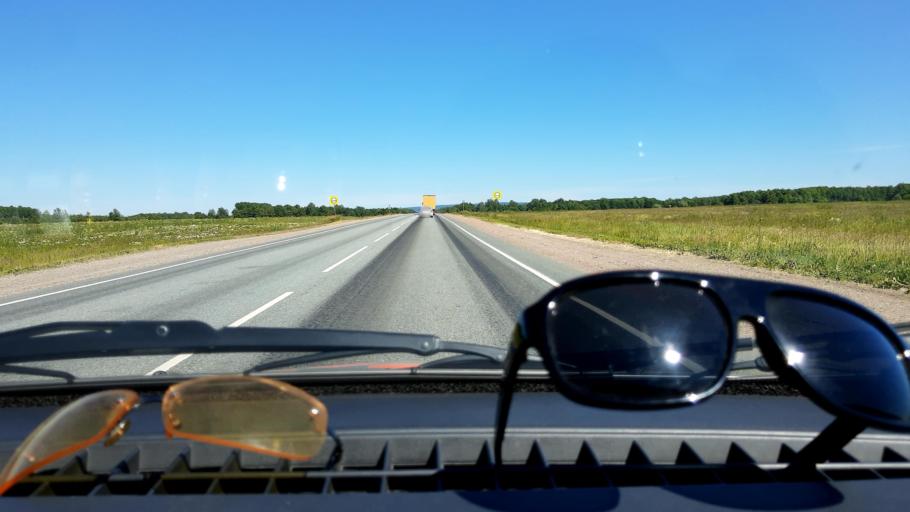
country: RU
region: Bashkortostan
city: Kudeyevskiy
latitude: 54.8173
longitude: 56.8133
